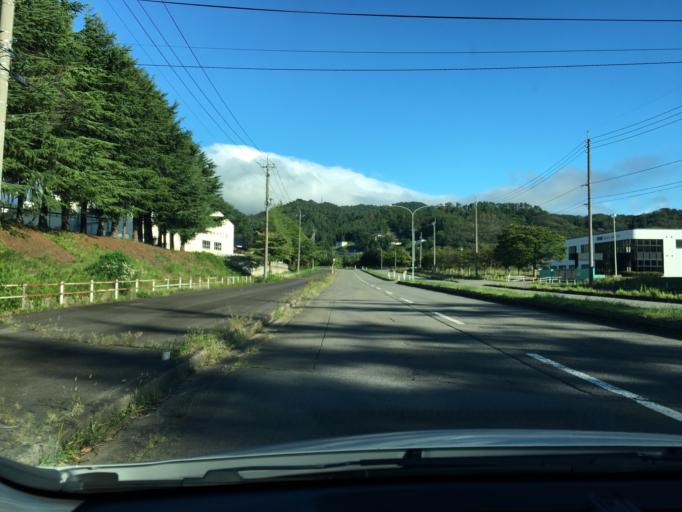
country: JP
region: Yamagata
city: Yonezawa
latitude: 37.9102
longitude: 140.1717
